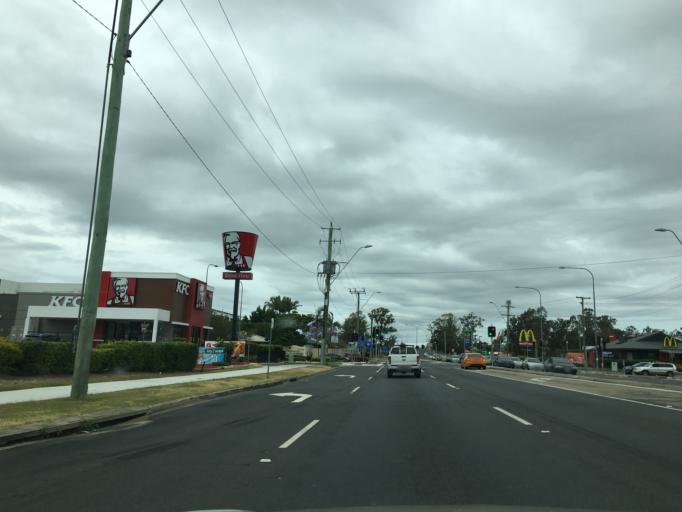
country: AU
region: Queensland
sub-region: Logan
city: Slacks Creek
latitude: -27.6670
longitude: 153.1397
